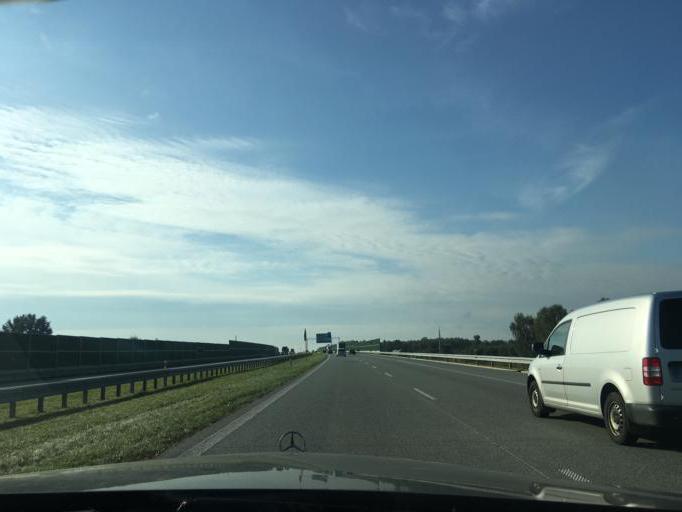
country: PL
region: Lodz Voivodeship
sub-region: Powiat lodzki wschodni
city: Andrespol
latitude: 51.7586
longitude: 19.5951
